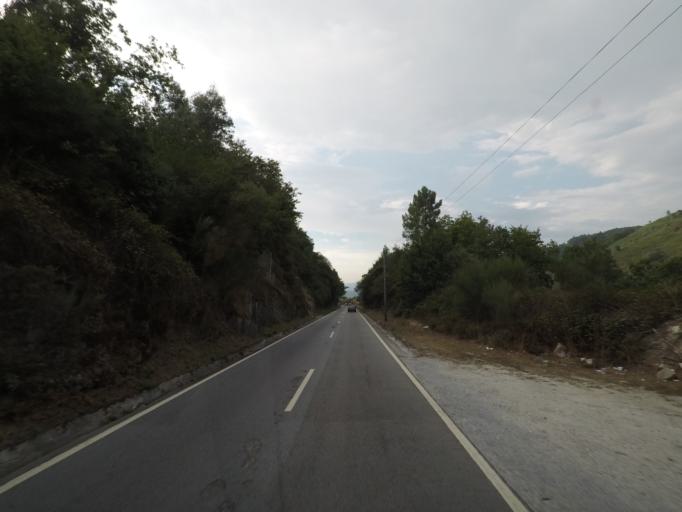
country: PT
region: Porto
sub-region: Baiao
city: Baiao
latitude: 41.2221
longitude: -7.9923
